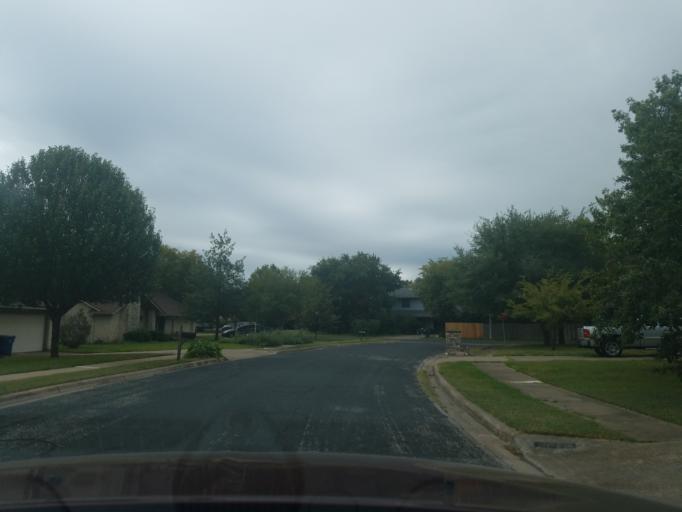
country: US
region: Texas
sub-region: Williamson County
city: Anderson Mill
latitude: 30.4641
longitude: -97.8055
